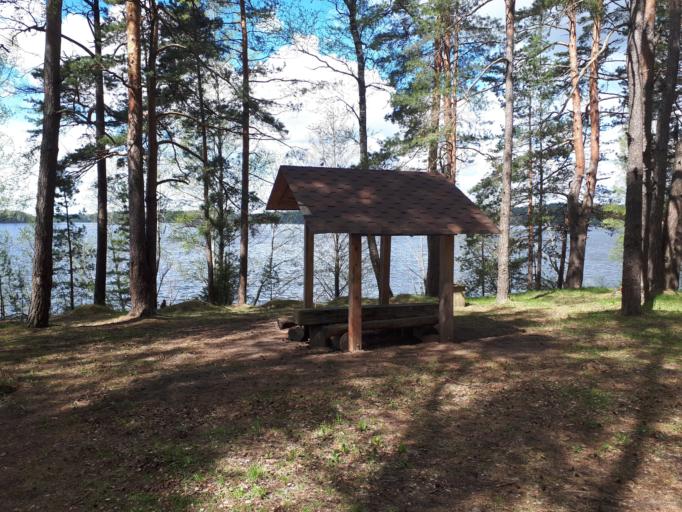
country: LT
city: Zarasai
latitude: 55.6292
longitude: 25.9564
